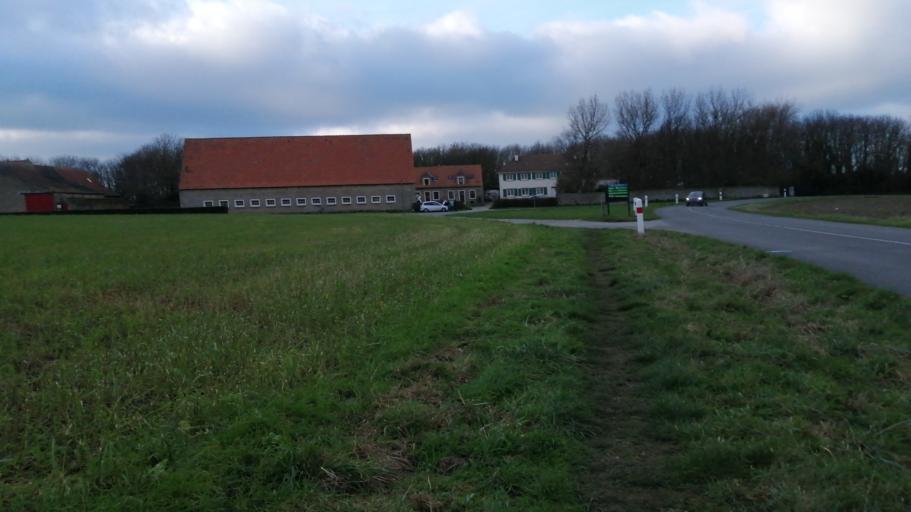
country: FR
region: Nord-Pas-de-Calais
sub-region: Departement du Pas-de-Calais
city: Ambleteuse
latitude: 50.8540
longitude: 1.5931
